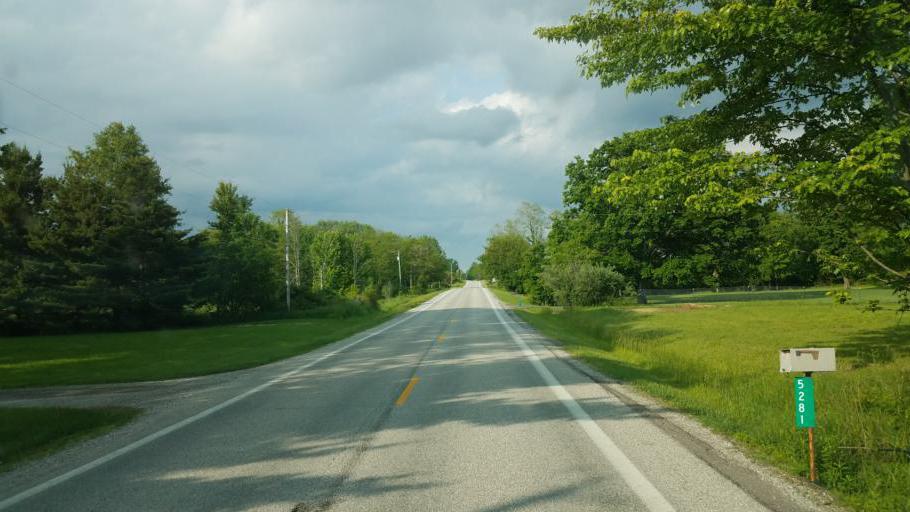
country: US
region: Ohio
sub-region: Knox County
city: Centerburg
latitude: 40.3542
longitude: -82.7704
